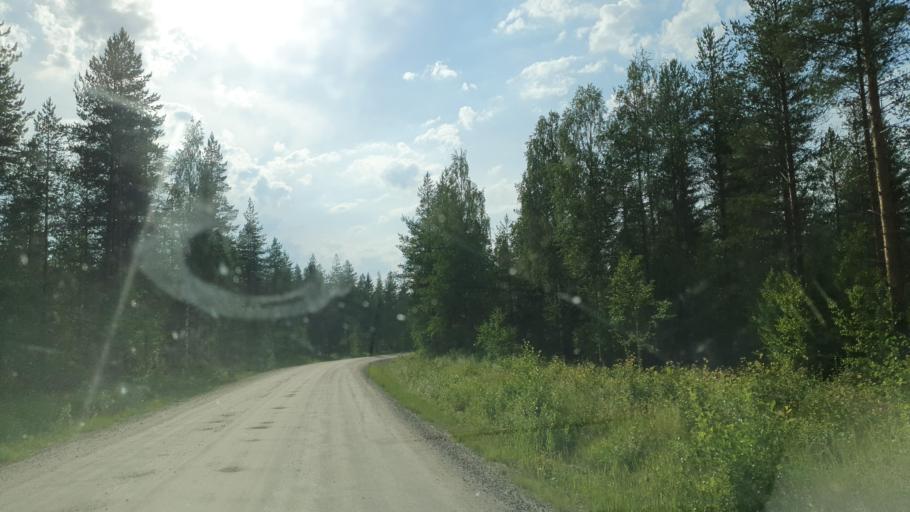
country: FI
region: Kainuu
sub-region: Kehys-Kainuu
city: Kuhmo
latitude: 64.0911
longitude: 29.5855
